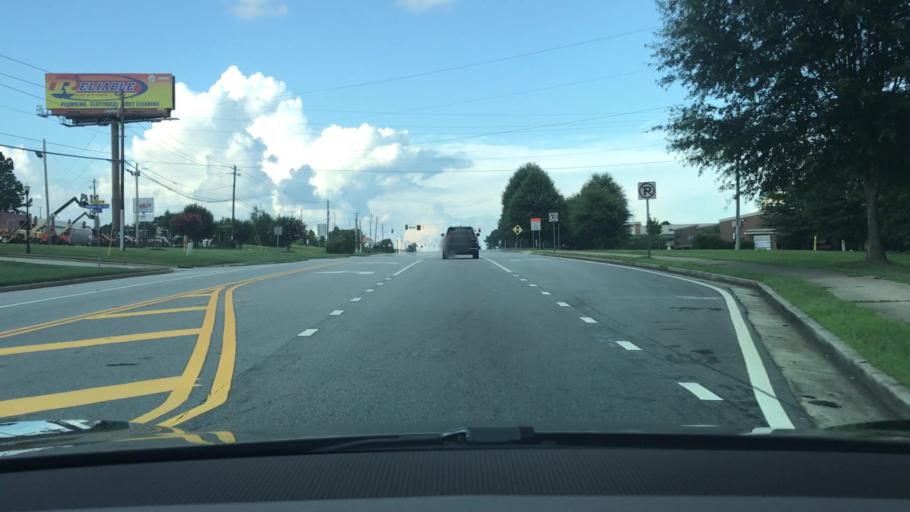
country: US
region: Georgia
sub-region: Gwinnett County
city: Sugar Hill
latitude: 34.0929
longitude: -84.0162
